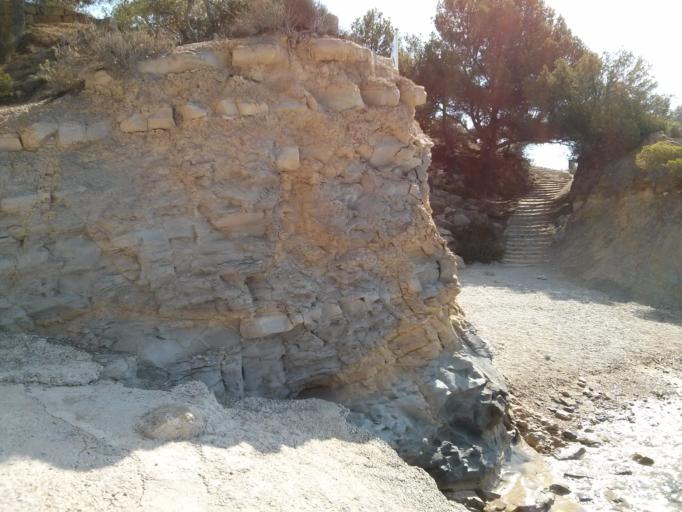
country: ES
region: Valencia
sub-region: Provincia de Alicante
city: Moraira
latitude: 38.6663
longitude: 0.0904
